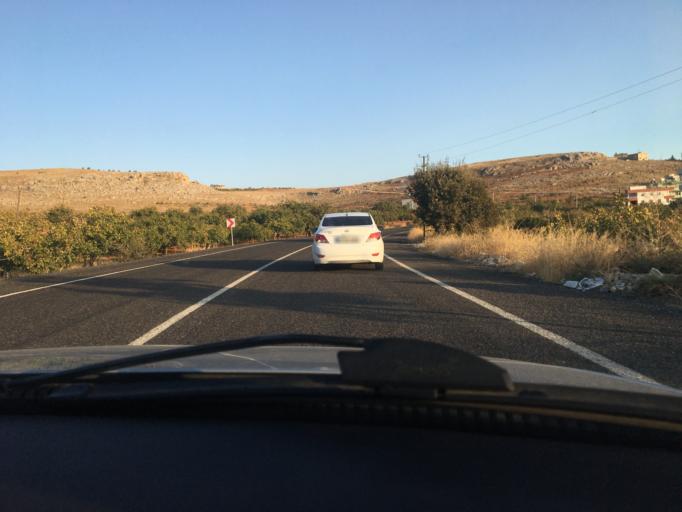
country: TR
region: Sanliurfa
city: Halfeti
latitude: 37.2157
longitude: 37.9609
